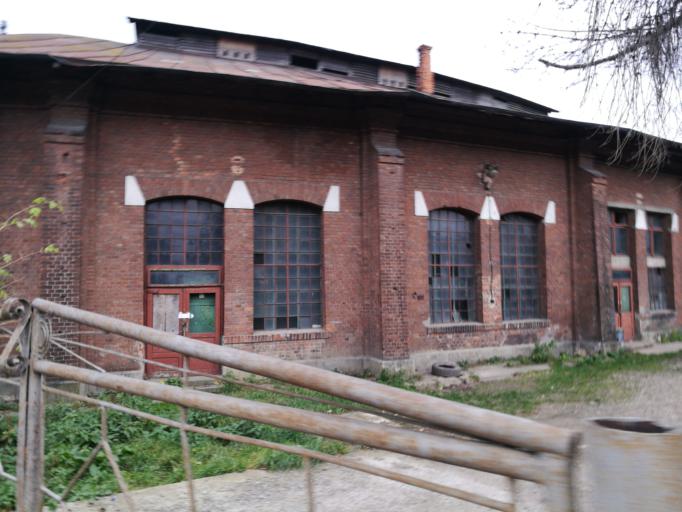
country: RO
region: Suceava
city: Suceava
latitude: 47.6691
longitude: 26.2718
